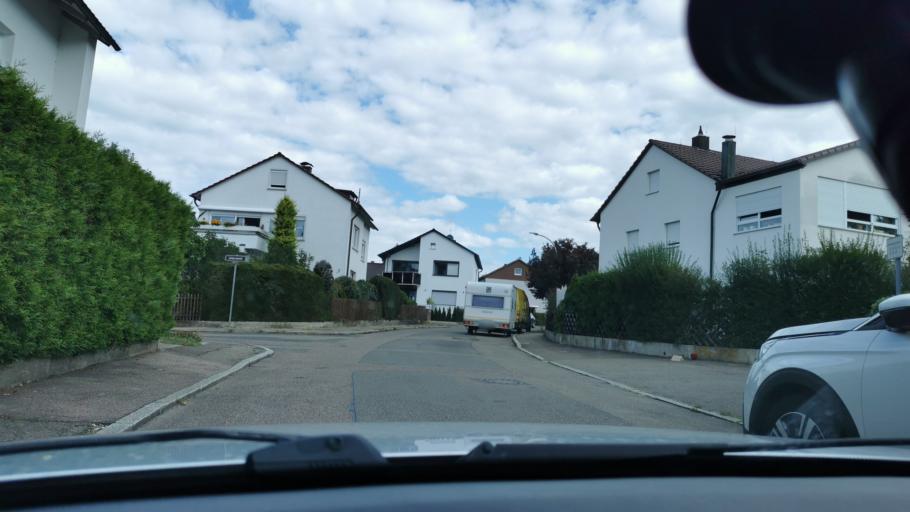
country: DE
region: Baden-Wuerttemberg
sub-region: Regierungsbezirk Stuttgart
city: Goeppingen
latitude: 48.7125
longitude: 9.6388
